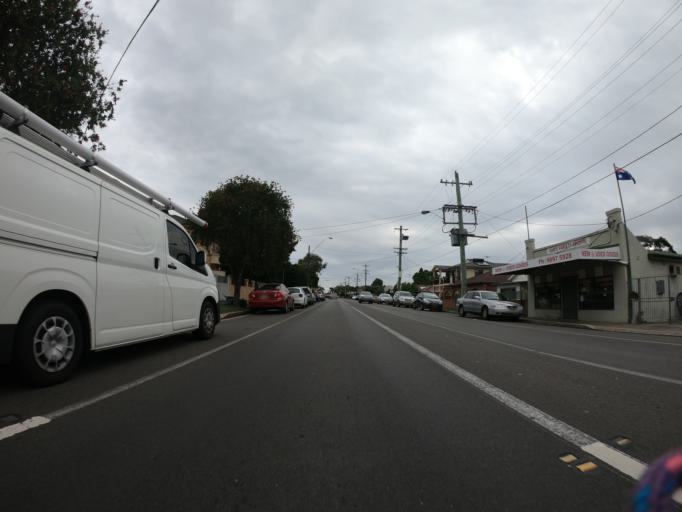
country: AU
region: New South Wales
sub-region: Parramatta
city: Granville
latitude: -33.8447
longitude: 151.0098
